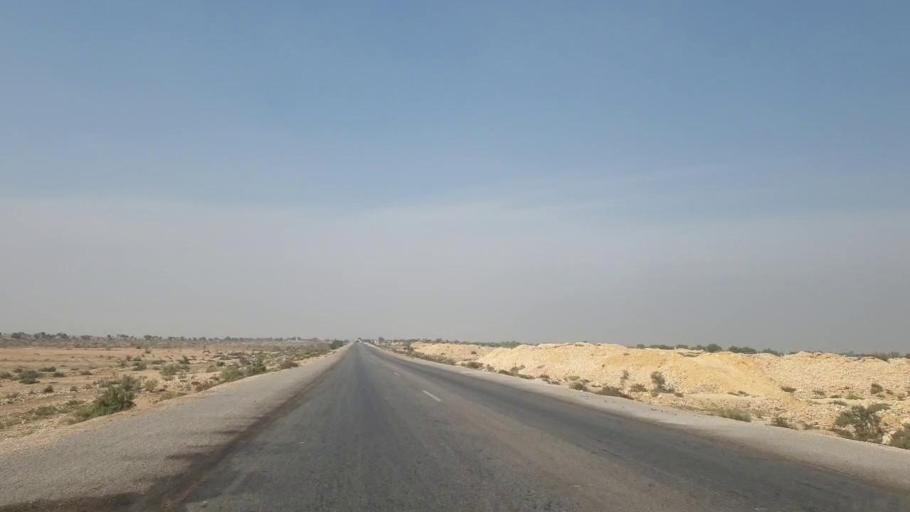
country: PK
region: Sindh
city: Hala
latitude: 25.8661
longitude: 68.2587
